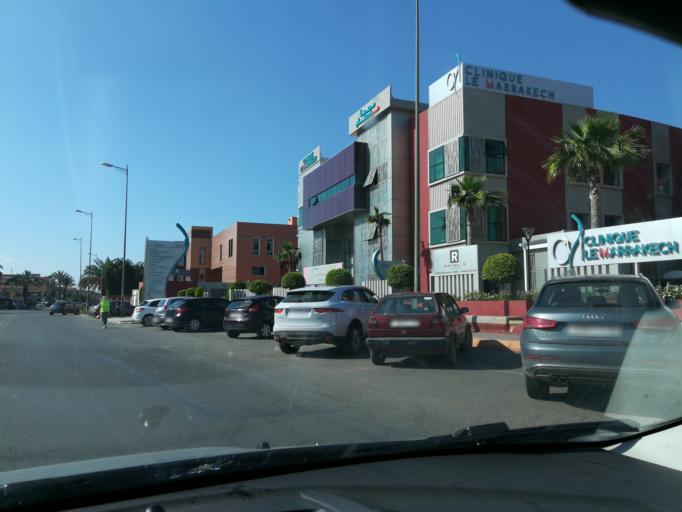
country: MA
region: Marrakech-Tensift-Al Haouz
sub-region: Marrakech
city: Marrakesh
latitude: 31.6533
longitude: -8.0513
